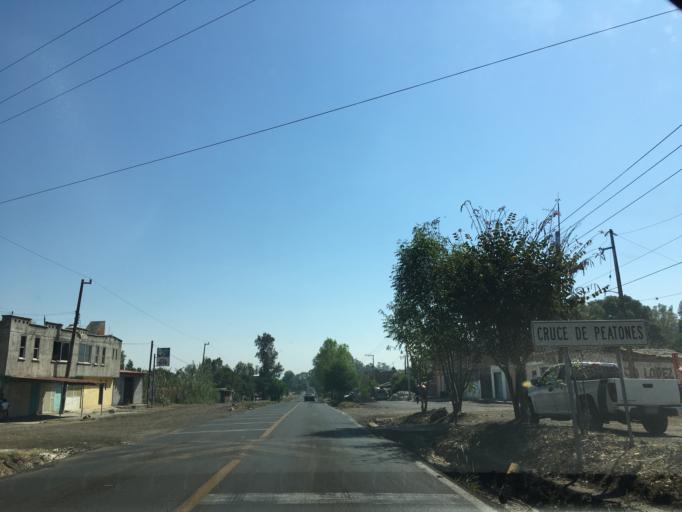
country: MX
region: Michoacan
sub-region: Indaparapeo
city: Colonia de Guadalupe
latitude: 19.7991
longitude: -100.9166
